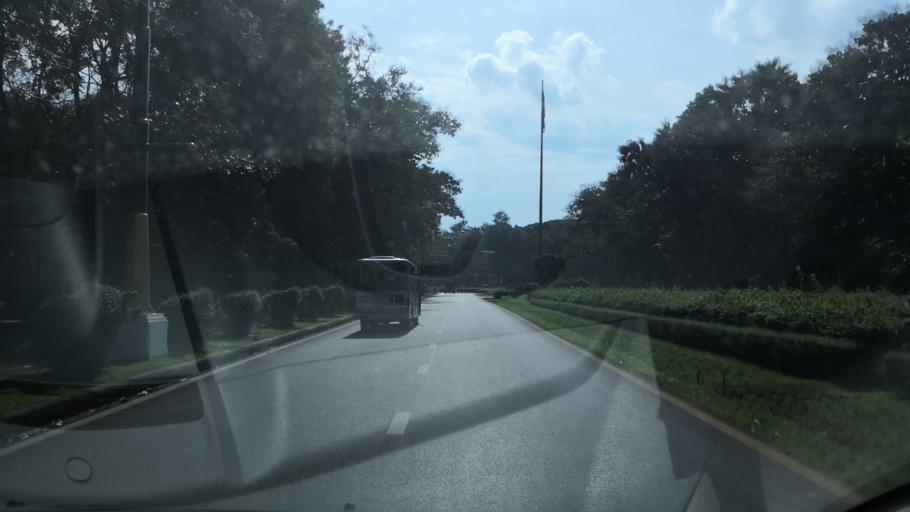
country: TH
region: Chiang Mai
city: Chiang Mai
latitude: 18.8072
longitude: 98.9541
